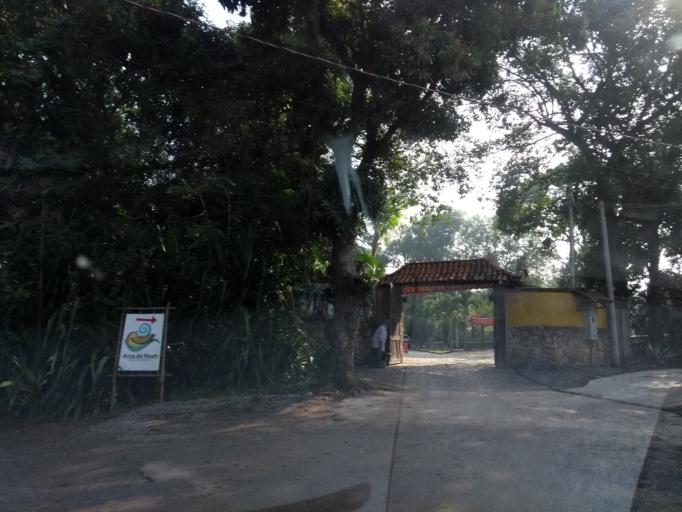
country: BR
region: Rio de Janeiro
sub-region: Itaguai
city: Itaguai
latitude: -22.9650
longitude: -43.6386
